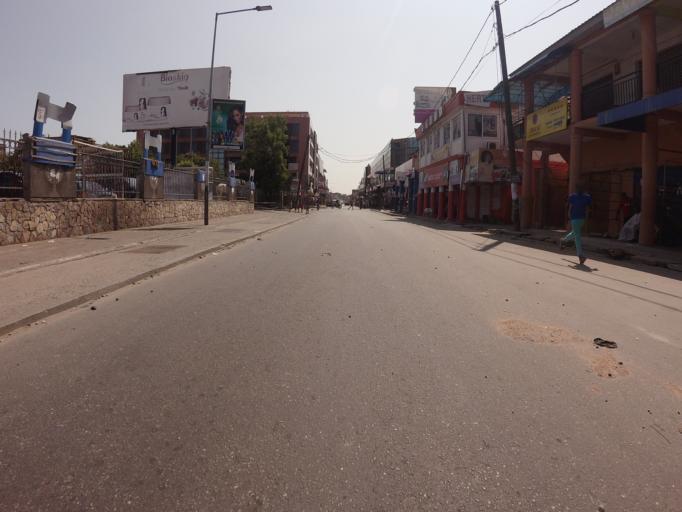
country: GH
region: Greater Accra
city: Accra
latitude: 5.5458
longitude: -0.2093
